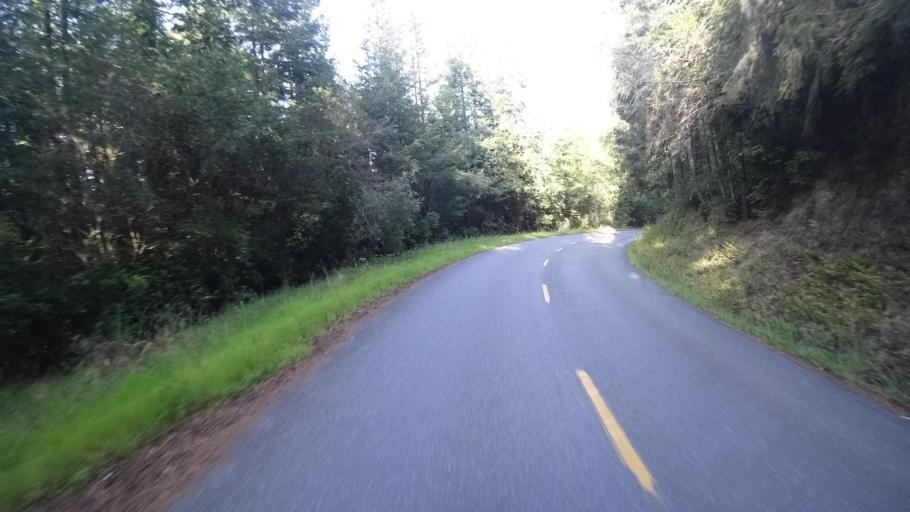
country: US
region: California
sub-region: Humboldt County
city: Bayside
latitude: 40.7564
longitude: -124.0339
